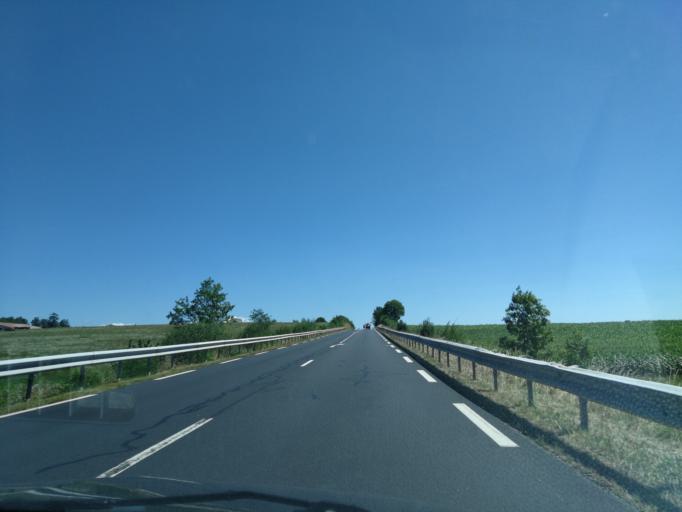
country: FR
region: Auvergne
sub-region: Departement du Cantal
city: Ytrac
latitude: 44.9334
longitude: 2.3633
